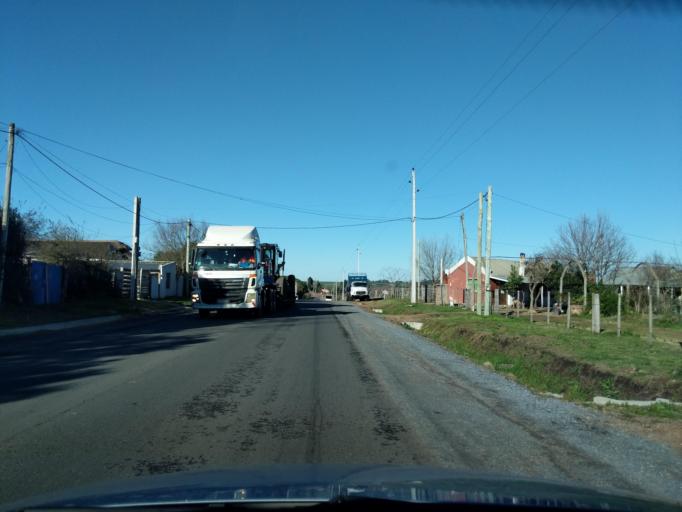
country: UY
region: Florida
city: Florida
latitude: -34.0989
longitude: -56.2412
